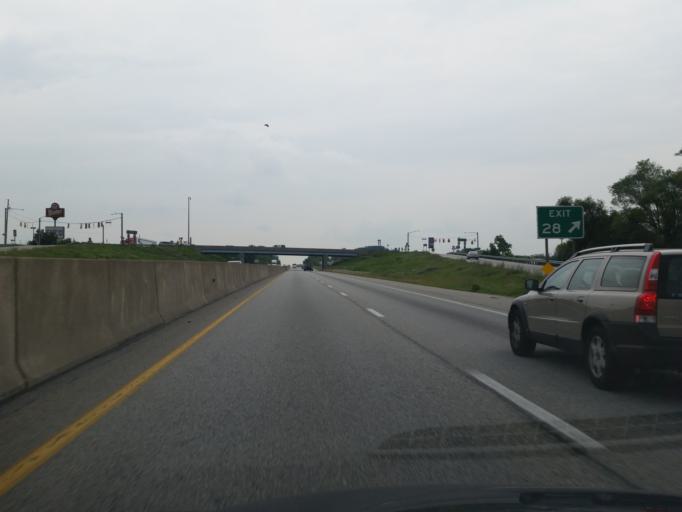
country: US
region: Pennsylvania
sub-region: York County
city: Manchester
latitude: 40.0802
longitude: -76.7639
